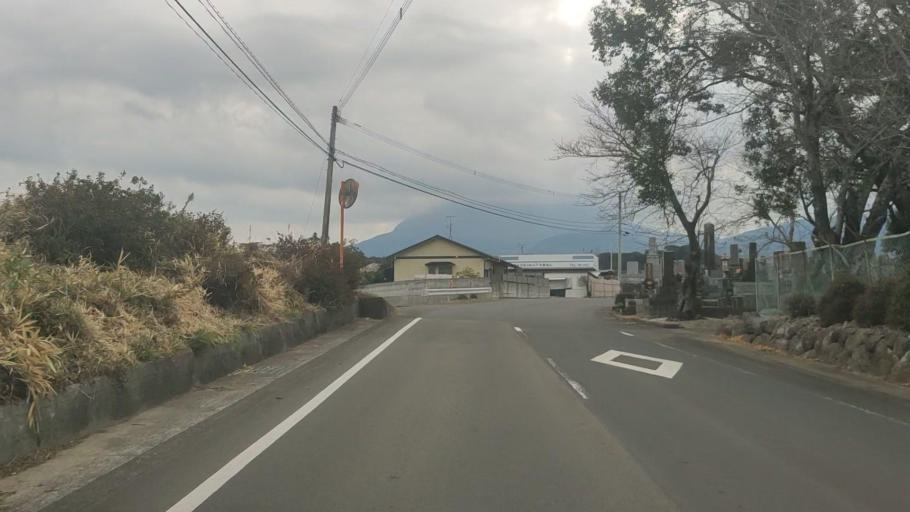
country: JP
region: Nagasaki
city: Shimabara
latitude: 32.8414
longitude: 130.2964
